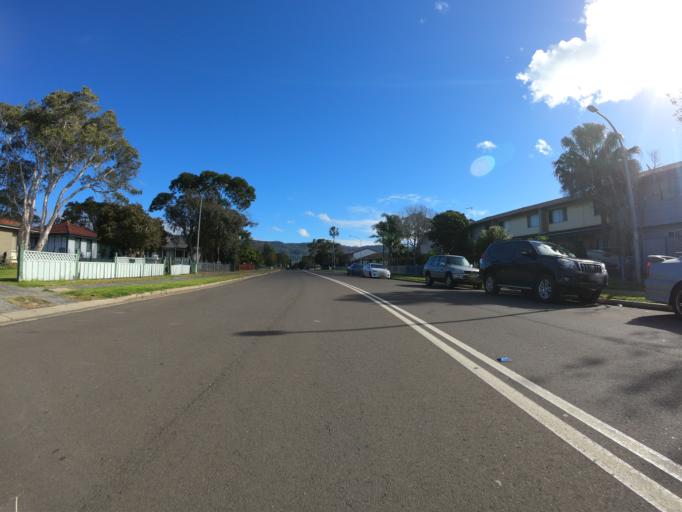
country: AU
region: New South Wales
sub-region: Wollongong
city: East Corrimal
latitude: -34.3666
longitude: 150.9220
